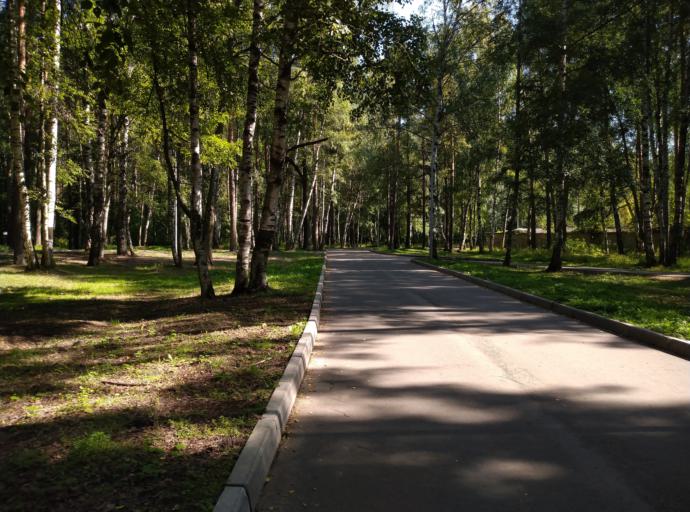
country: RU
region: Kostroma
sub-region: Kostromskoy Rayon
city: Kostroma
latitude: 57.7934
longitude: 40.9645
